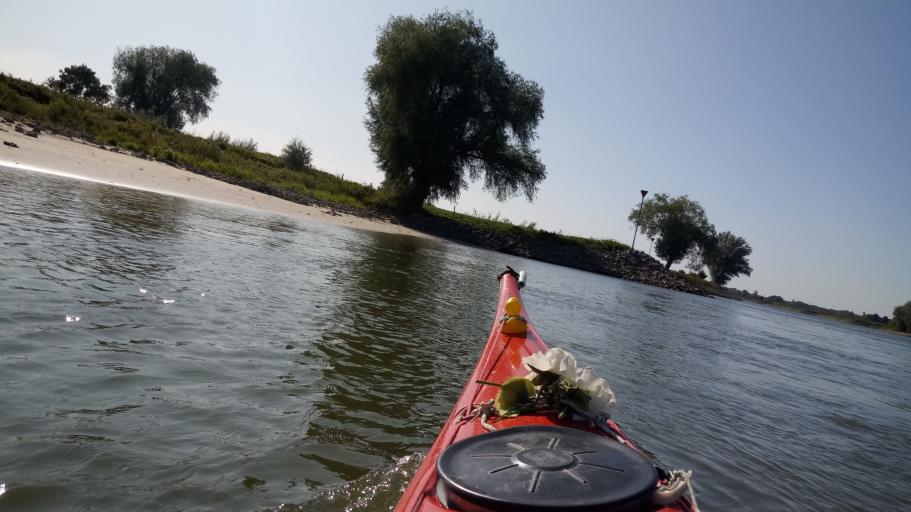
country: NL
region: Gelderland
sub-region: Gemeente Lochem
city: Gorssel
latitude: 52.2037
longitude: 6.1832
